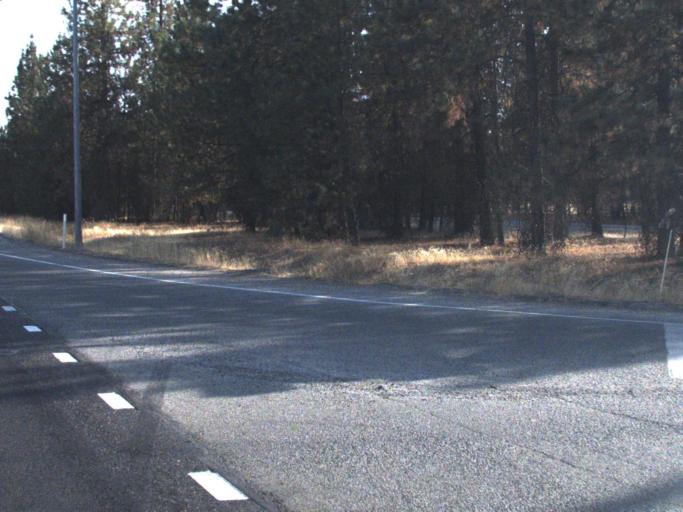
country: US
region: Washington
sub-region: Spokane County
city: Mead
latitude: 47.8378
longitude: -117.3542
